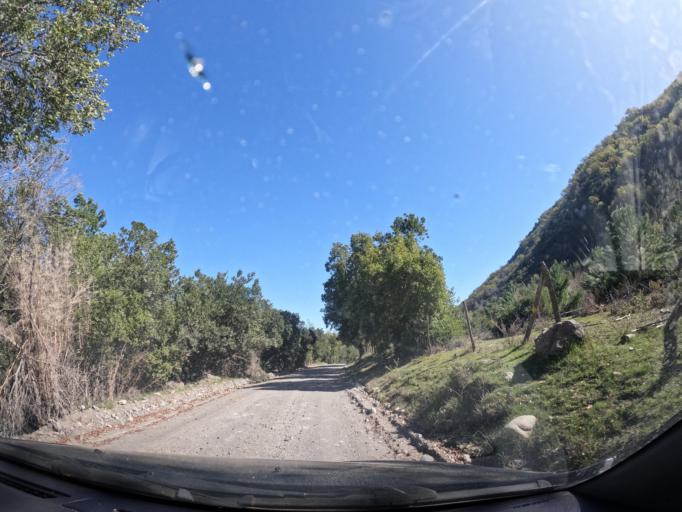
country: CL
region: Maule
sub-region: Provincia de Linares
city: Longavi
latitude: -36.2290
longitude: -71.3986
